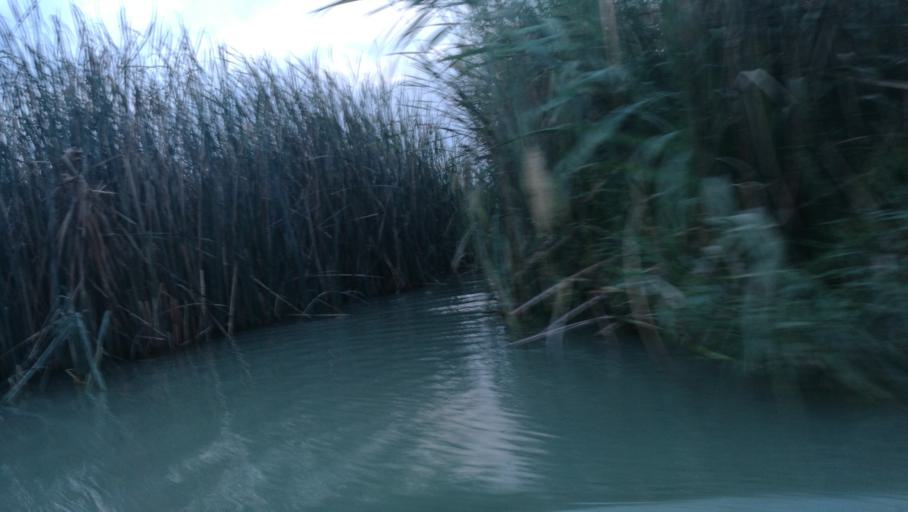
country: IQ
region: Dhi Qar
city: Al Jabayish
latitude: 30.9820
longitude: 47.0367
